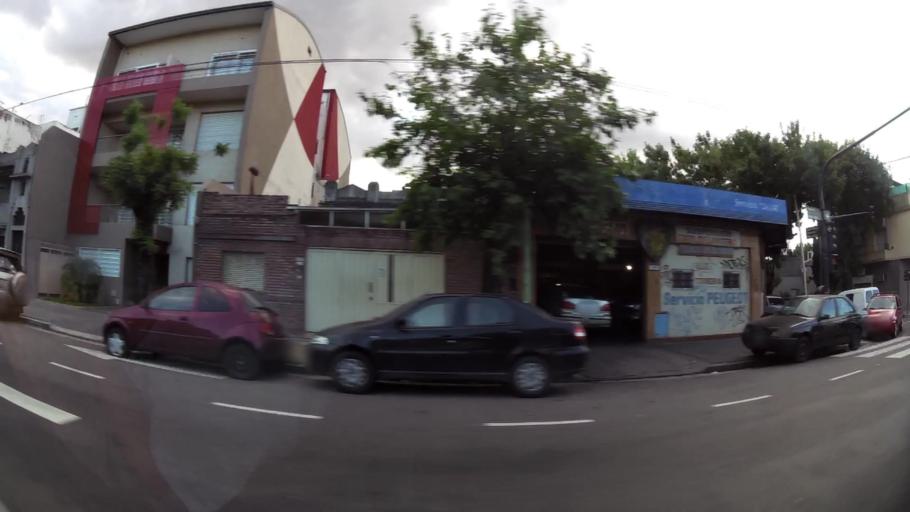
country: AR
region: Buenos Aires F.D.
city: Colegiales
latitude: -34.5624
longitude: -58.4835
